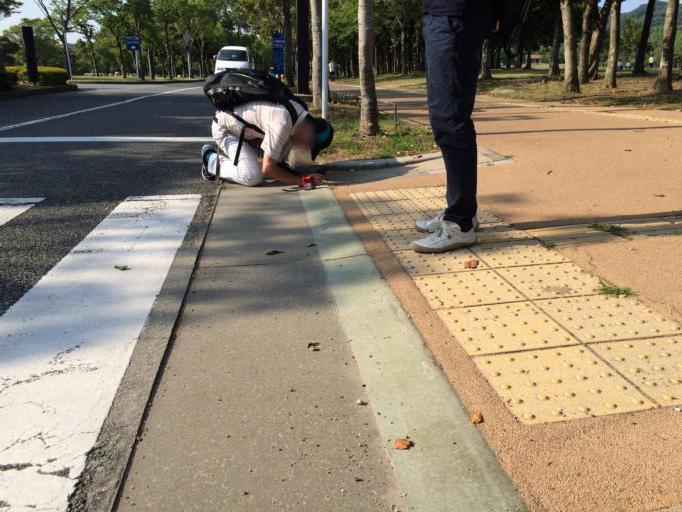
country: JP
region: Hyogo
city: Kobe
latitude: 34.7081
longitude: 135.1133
